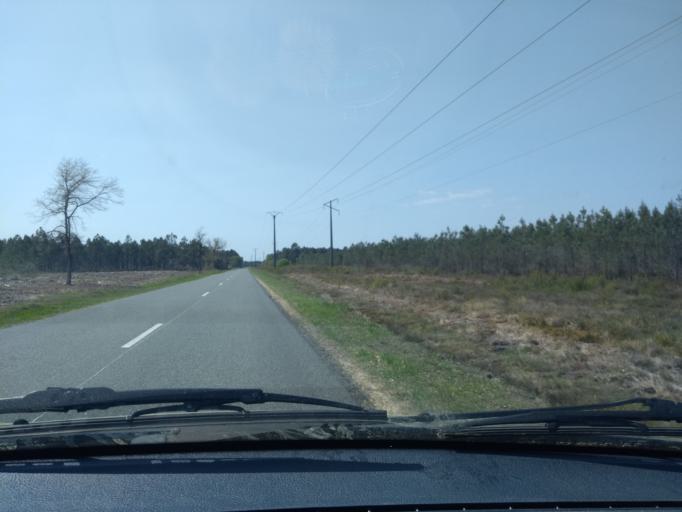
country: FR
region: Aquitaine
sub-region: Departement de la Gironde
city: Belin-Beliet
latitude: 44.5275
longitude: -0.7157
